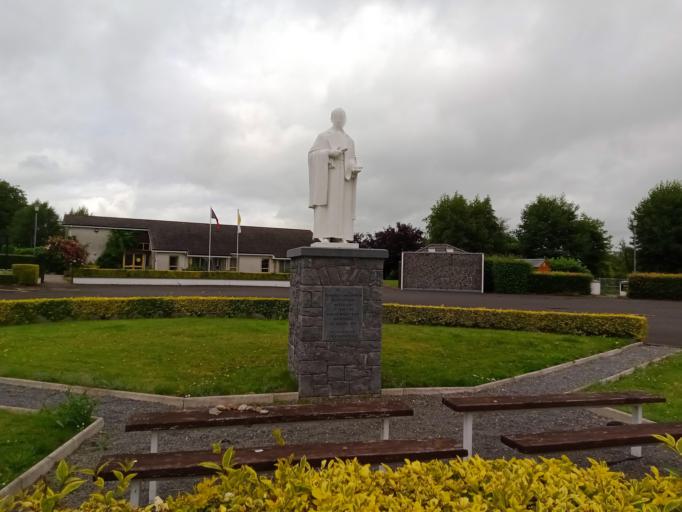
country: IE
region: Leinster
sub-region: Kilkenny
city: Callan
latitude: 52.5521
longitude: -7.3979
